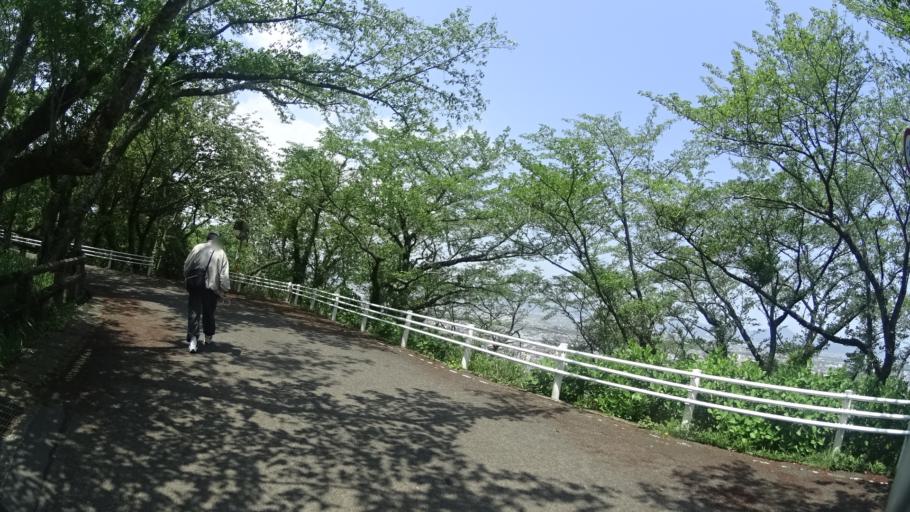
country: JP
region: Tokushima
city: Tokushima-shi
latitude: 34.0693
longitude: 134.5142
